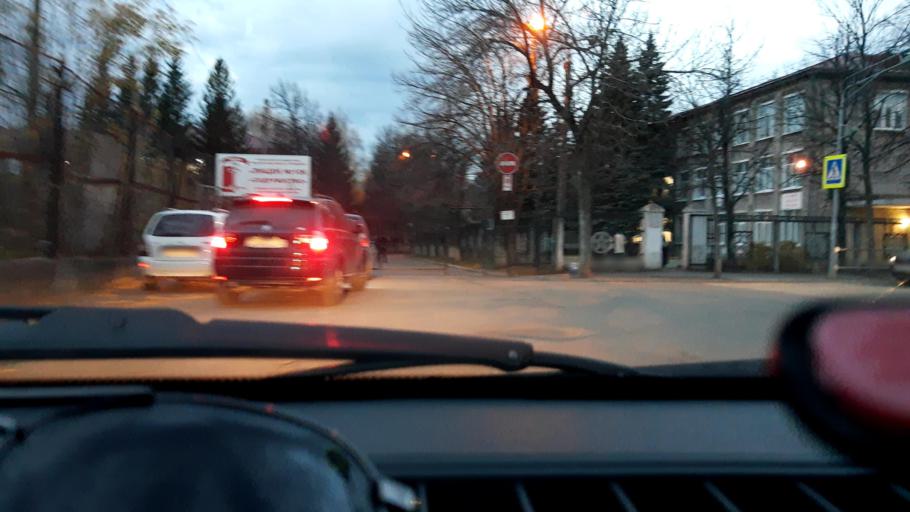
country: RU
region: Bashkortostan
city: Ufa
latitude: 54.7781
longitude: 56.0267
